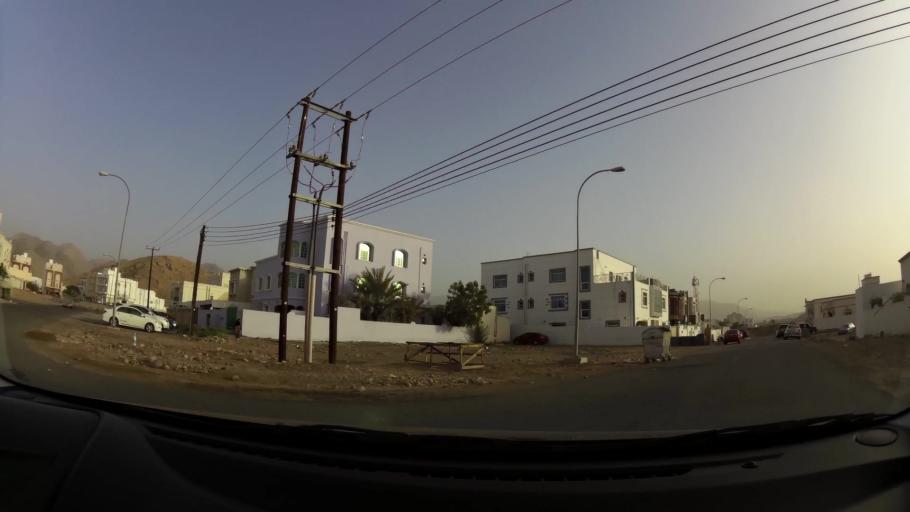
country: OM
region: Muhafazat Masqat
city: Bawshar
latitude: 23.5117
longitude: 58.3445
